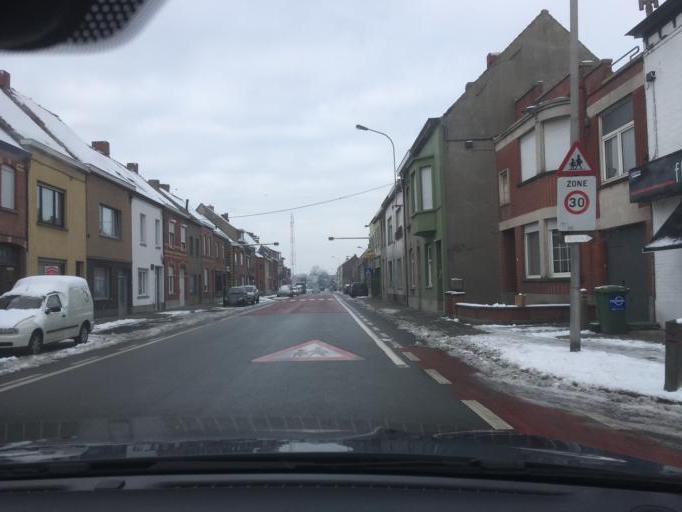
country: BE
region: Flanders
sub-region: Provincie West-Vlaanderen
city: Kortrijk
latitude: 50.8347
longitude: 3.2517
